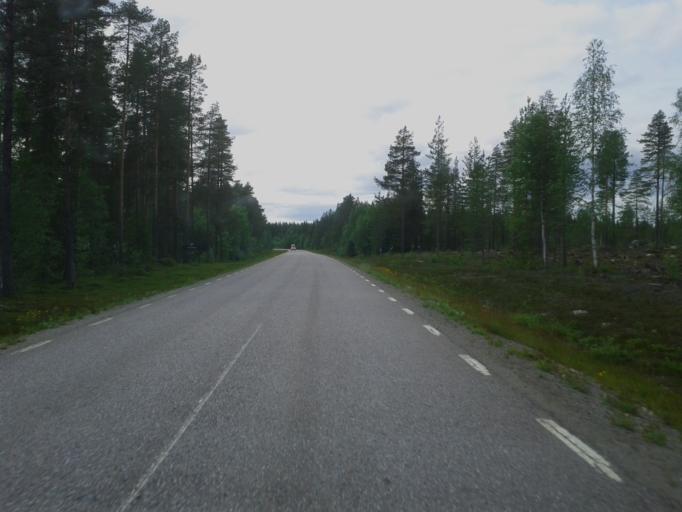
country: SE
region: Vaesterbotten
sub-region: Sorsele Kommun
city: Sorsele
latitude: 65.2896
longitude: 17.8190
